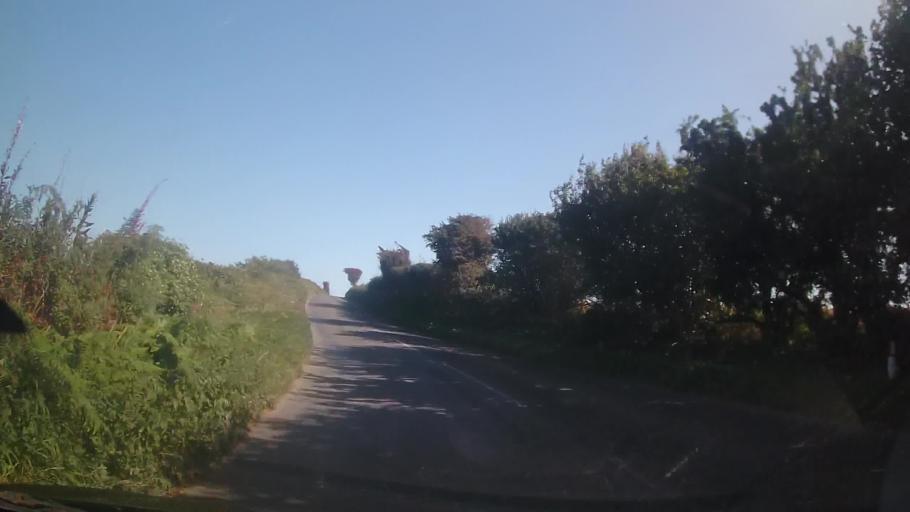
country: GB
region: Wales
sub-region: Pembrokeshire
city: Mathry
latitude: 51.9359
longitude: -5.0431
